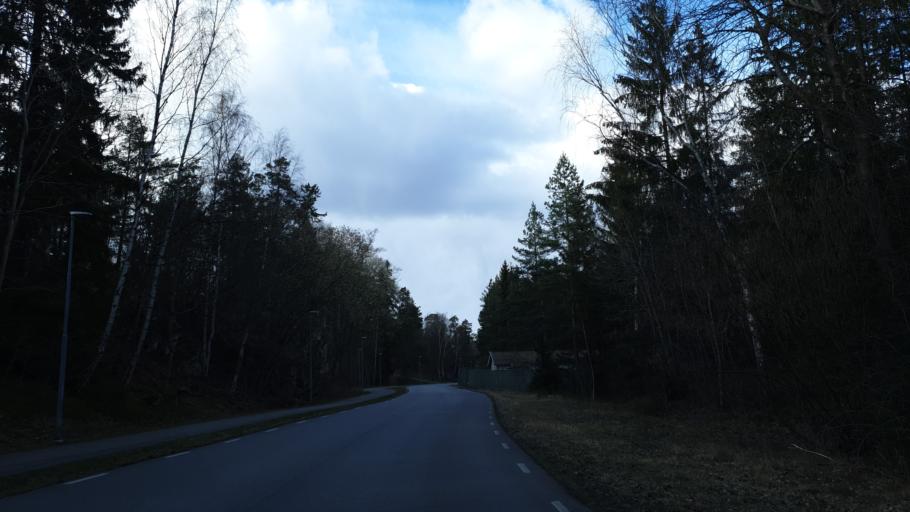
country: SE
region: Stockholm
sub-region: Lidingo
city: Lidingoe
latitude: 59.3844
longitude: 18.1186
